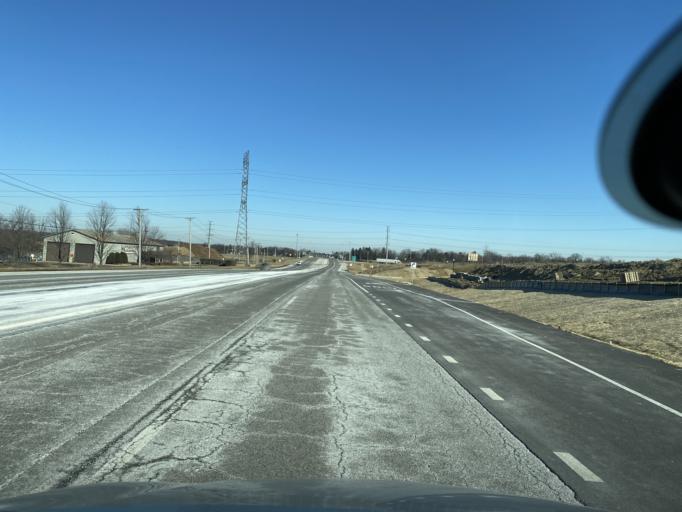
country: US
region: Illinois
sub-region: Cook County
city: Lemont
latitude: 41.6313
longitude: -88.0162
